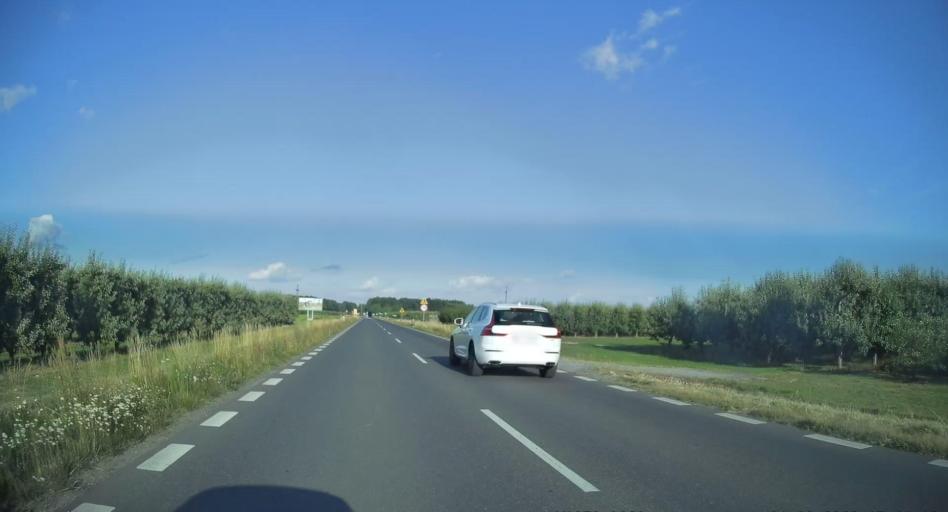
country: PL
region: Lodz Voivodeship
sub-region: Powiat rawski
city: Biala Rawska
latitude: 51.8065
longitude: 20.5721
